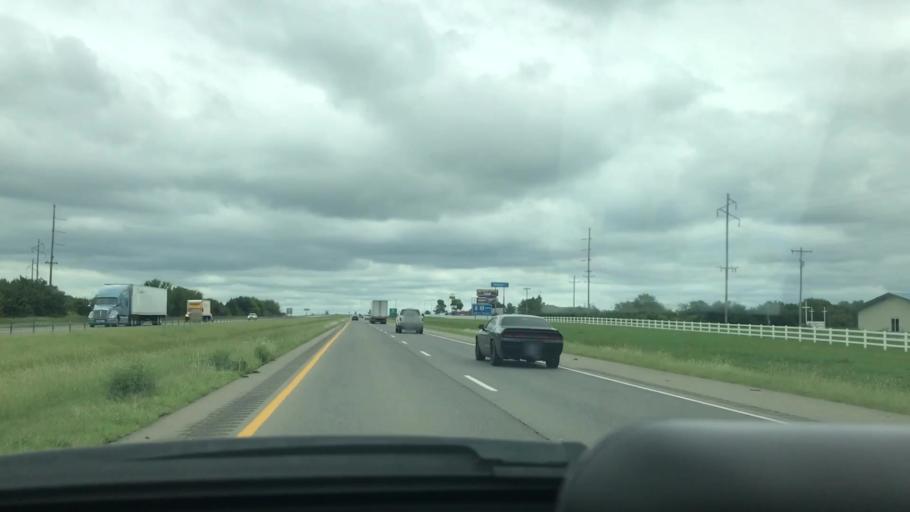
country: US
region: Oklahoma
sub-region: McIntosh County
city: Checotah
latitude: 35.4664
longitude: -95.5401
